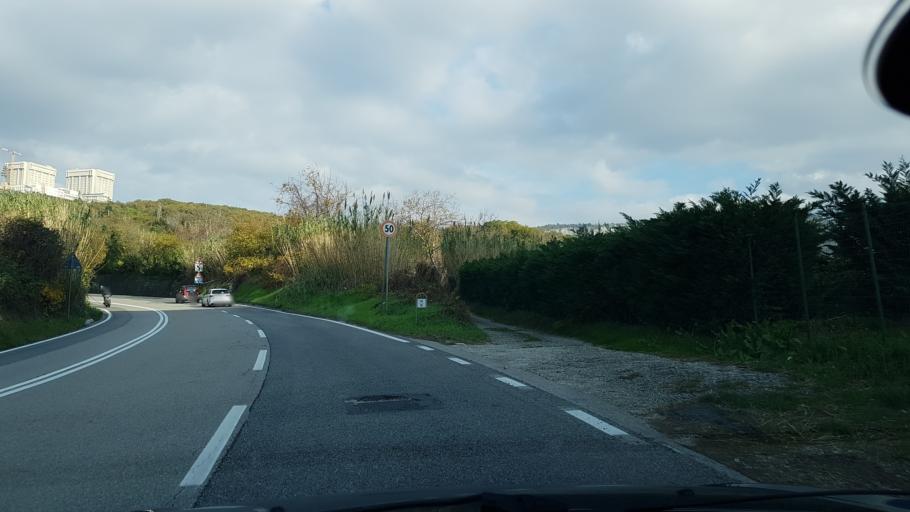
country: IT
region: Friuli Venezia Giulia
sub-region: Provincia di Trieste
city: Domio
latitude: 45.6228
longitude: 13.8214
